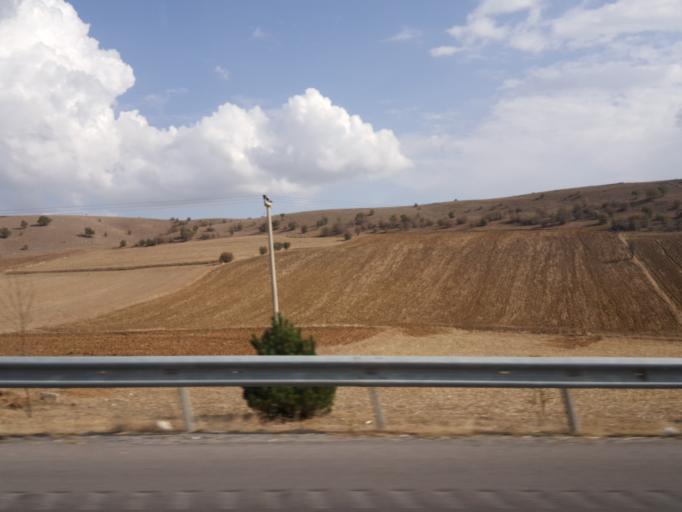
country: TR
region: Corum
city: Alaca
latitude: 40.2851
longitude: 34.6486
